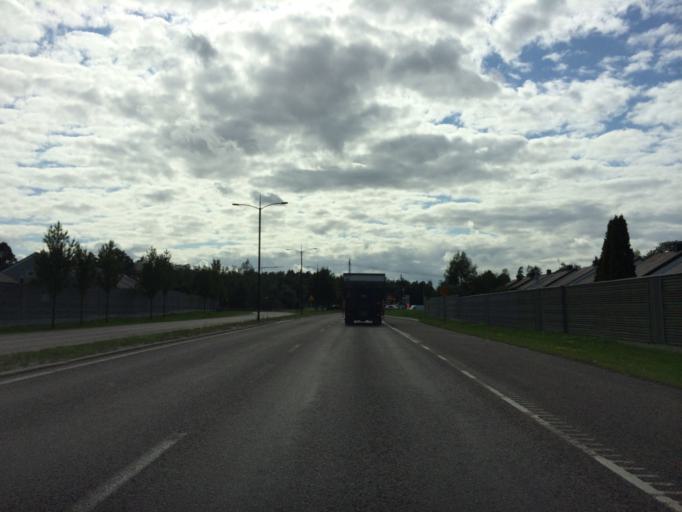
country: SE
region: Stockholm
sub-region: Sollentuna Kommun
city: Sollentuna
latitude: 59.4202
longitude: 17.9423
